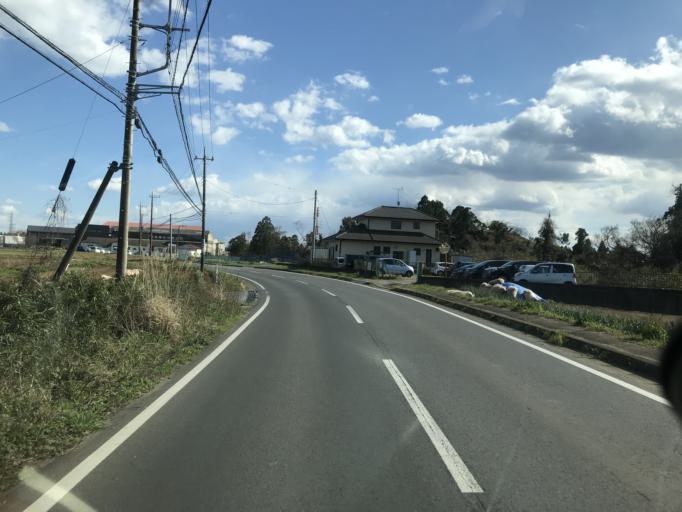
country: JP
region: Chiba
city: Sawara
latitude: 35.8762
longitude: 140.4179
